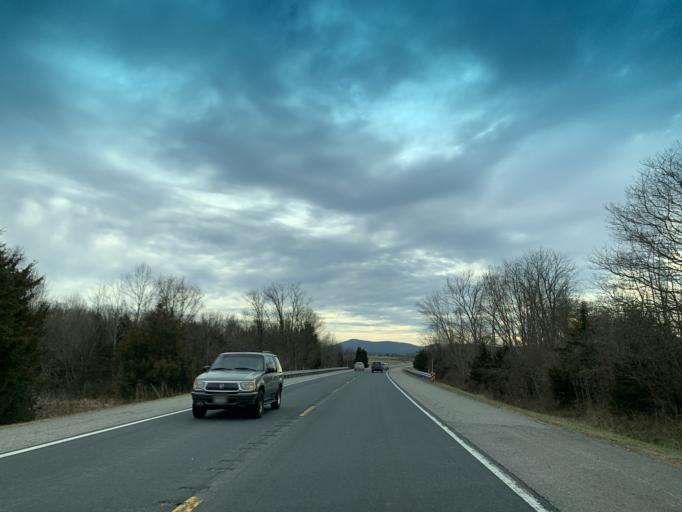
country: US
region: Maryland
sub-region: Washington County
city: Boonsboro
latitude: 39.4683
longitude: -77.6572
